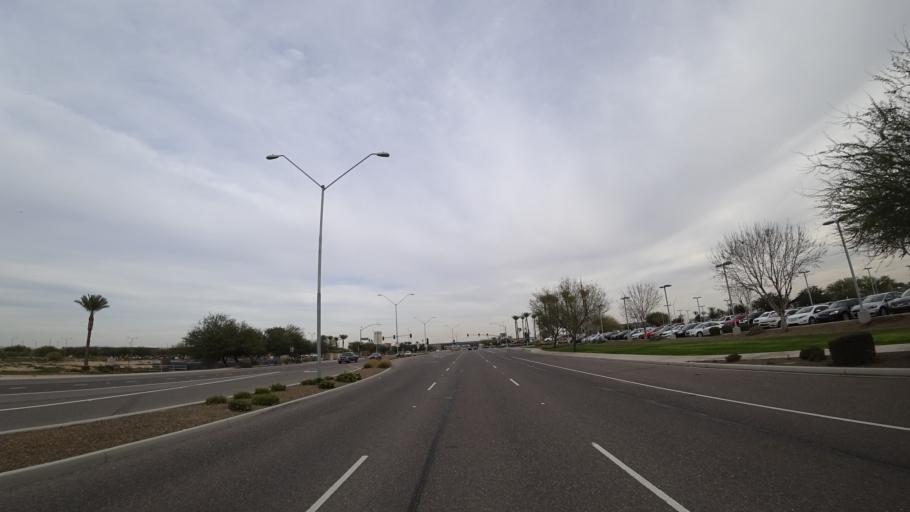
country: US
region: Arizona
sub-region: Maricopa County
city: Citrus Park
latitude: 33.6096
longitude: -112.4242
